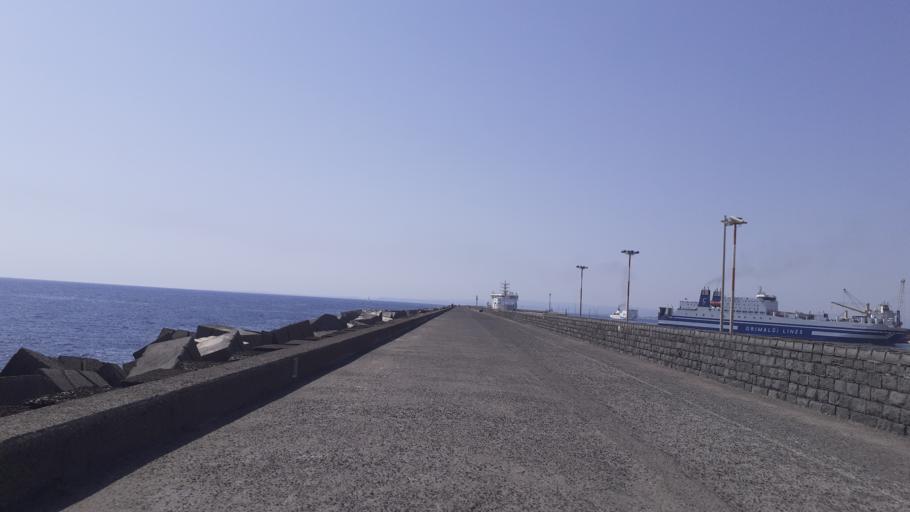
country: IT
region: Sicily
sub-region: Catania
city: Catania
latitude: 37.4989
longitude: 15.0992
